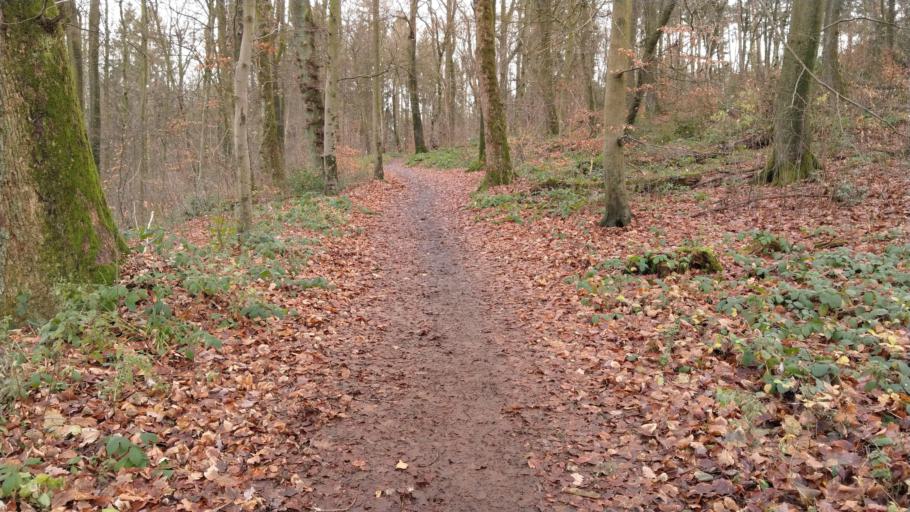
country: DE
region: North Rhine-Westphalia
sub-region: Regierungsbezirk Koln
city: Aachen
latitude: 50.7352
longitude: 6.0713
